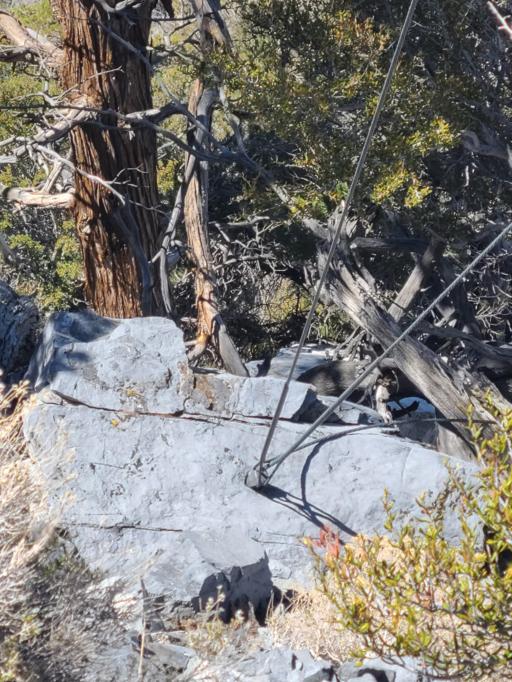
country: US
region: California
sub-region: San Bernardino County
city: Big Bear Lake
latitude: 34.3284
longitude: -116.9206
